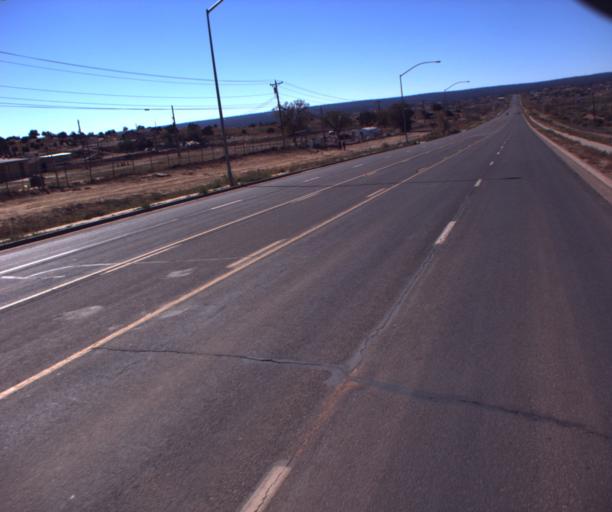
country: US
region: Arizona
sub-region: Apache County
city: Window Rock
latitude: 35.6615
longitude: -109.0681
